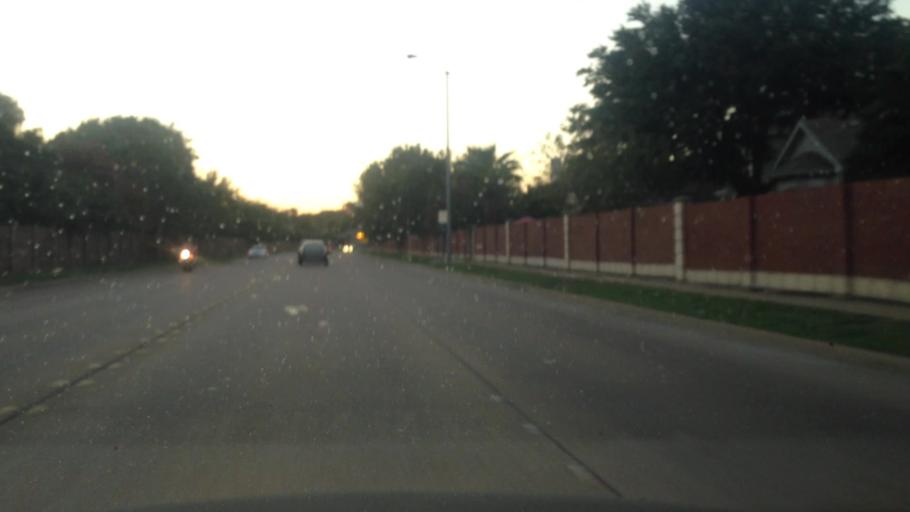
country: US
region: Texas
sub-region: Tarrant County
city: Watauga
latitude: 32.8549
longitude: -97.2783
